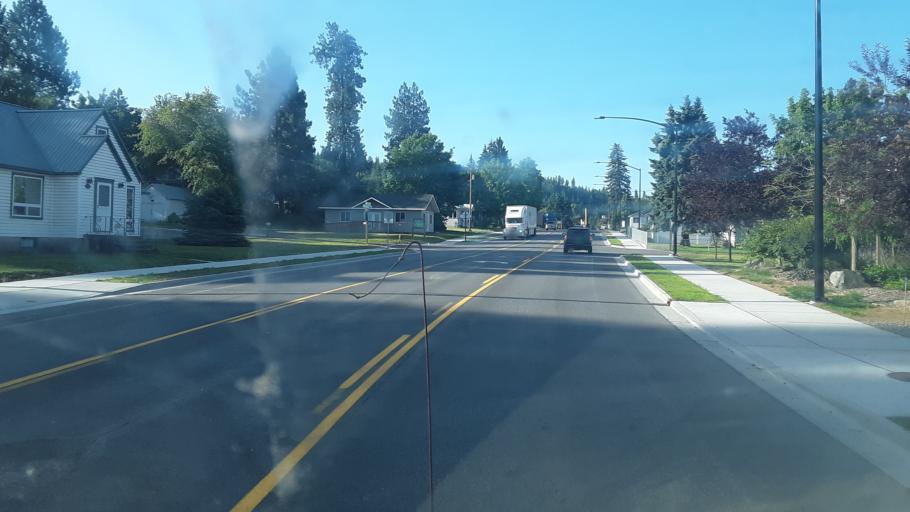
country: US
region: Idaho
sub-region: Boundary County
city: Bonners Ferry
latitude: 48.6911
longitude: -116.3164
